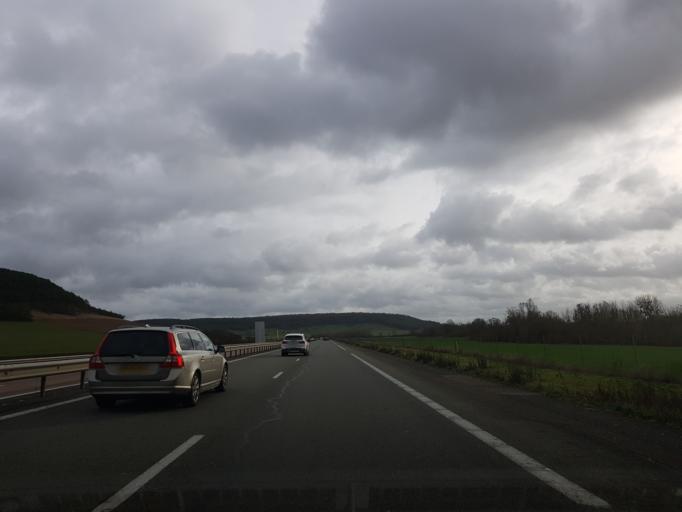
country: FR
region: Champagne-Ardenne
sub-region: Departement de la Haute-Marne
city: Chateauvillain
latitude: 48.0700
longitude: 4.8977
